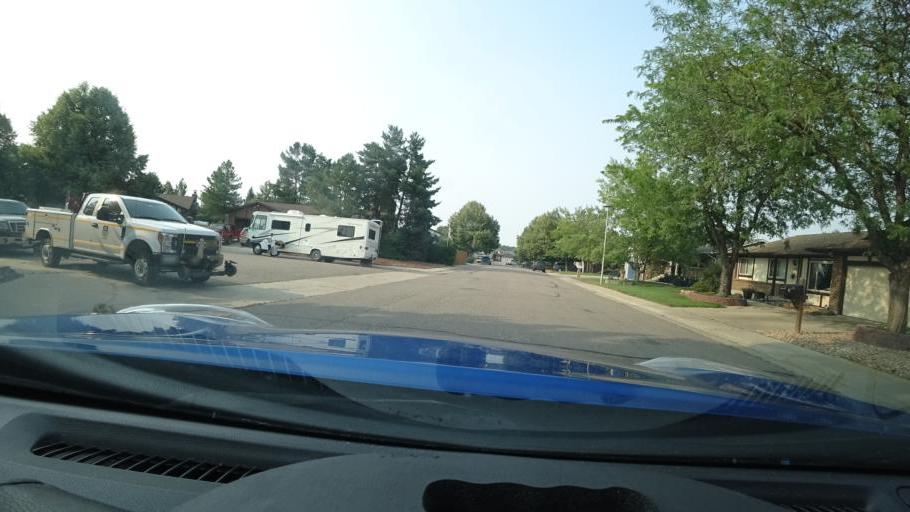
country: US
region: Colorado
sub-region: Adams County
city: Aurora
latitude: 39.6698
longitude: -104.7901
